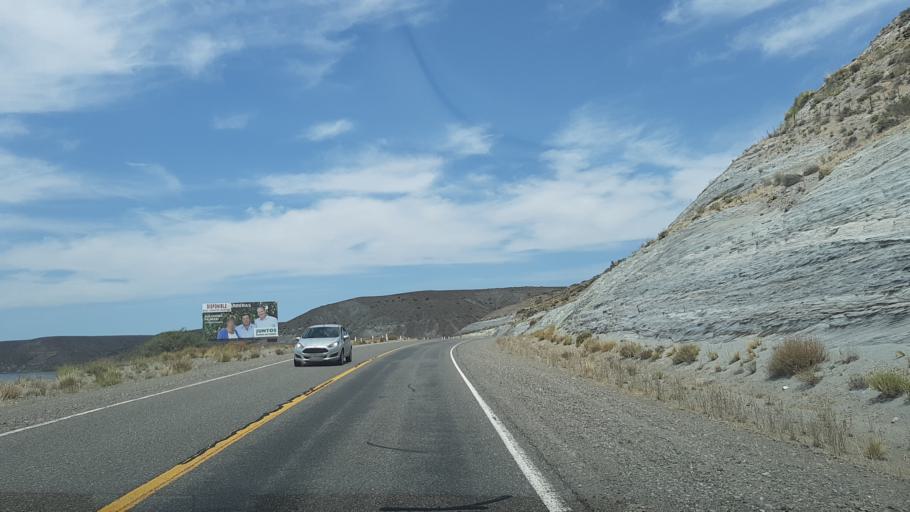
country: AR
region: Neuquen
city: Junin de los Andes
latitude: -40.4473
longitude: -70.6649
